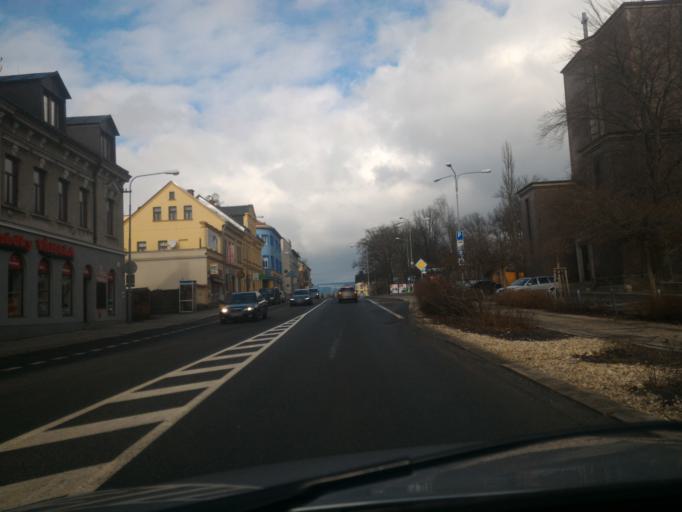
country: CZ
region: Liberecky
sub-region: Okres Jablonec nad Nisou
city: Jablonec nad Nisou
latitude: 50.7266
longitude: 15.1705
